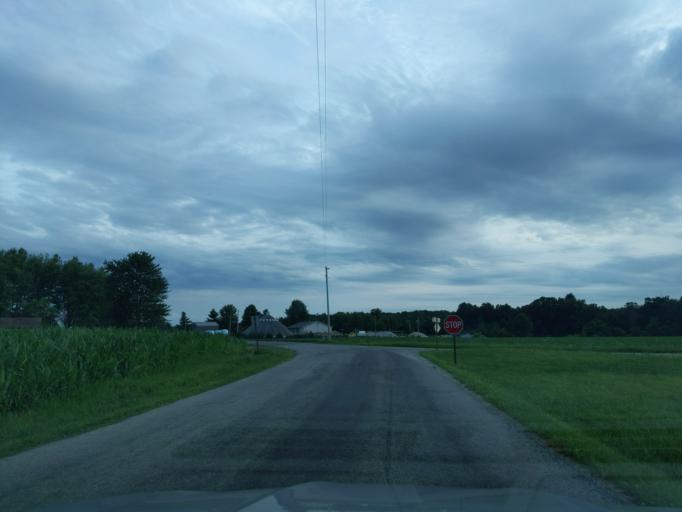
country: US
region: Indiana
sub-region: Ripley County
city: Sunman
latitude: 39.2859
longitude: -85.1009
